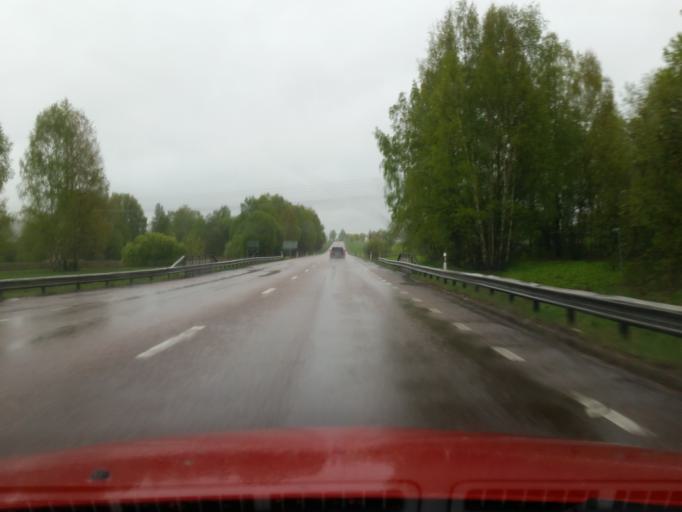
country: SE
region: Dalarna
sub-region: Borlange Kommun
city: Borlaenge
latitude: 60.4718
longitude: 15.4602
